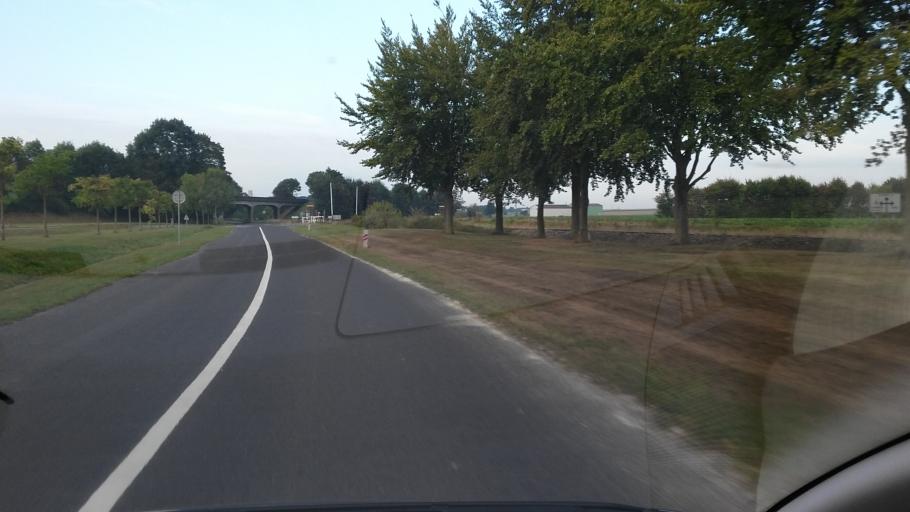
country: FR
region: Champagne-Ardenne
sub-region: Departement de la Marne
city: Connantre
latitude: 48.7344
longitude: 3.9300
